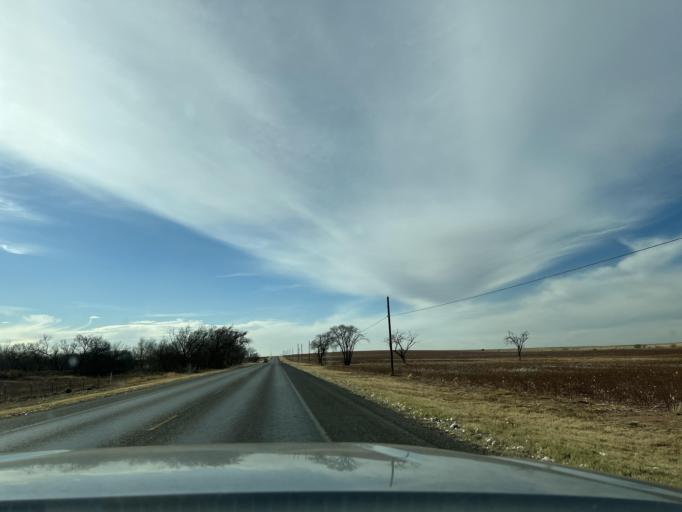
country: US
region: Texas
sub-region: Fisher County
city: Roby
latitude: 32.7409
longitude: -100.4791
